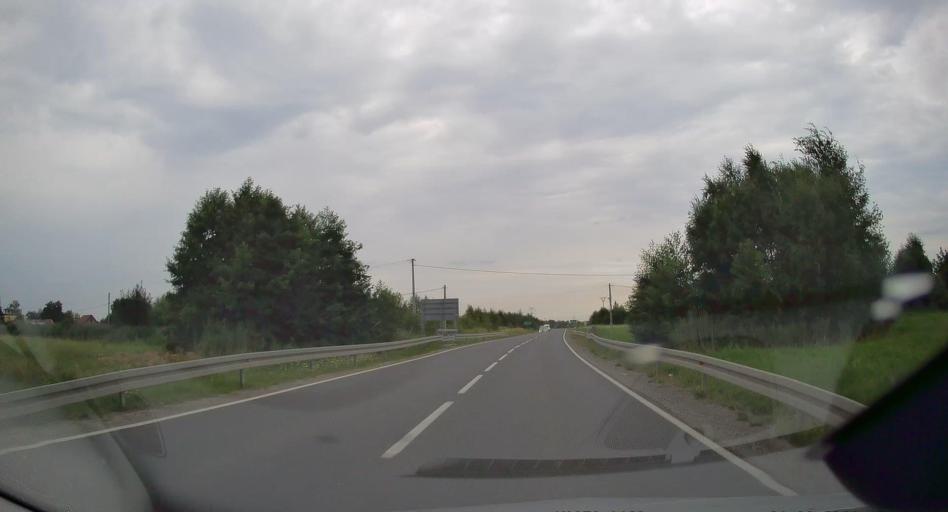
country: PL
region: Lesser Poland Voivodeship
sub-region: Powiat tarnowski
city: Wojnicz
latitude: 49.9758
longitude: 20.8425
